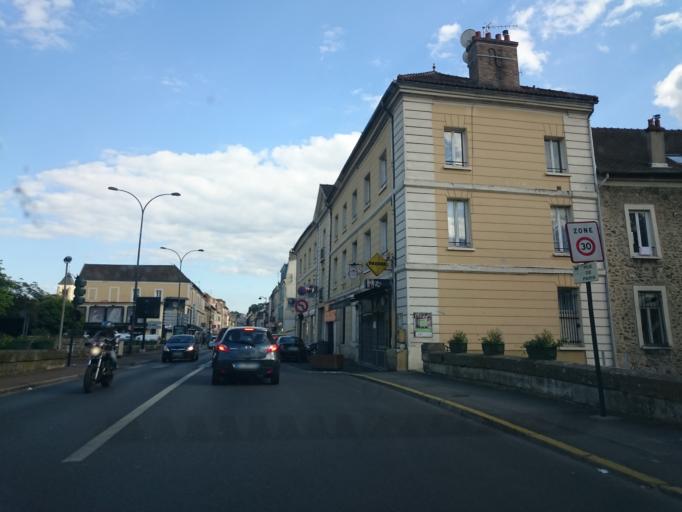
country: FR
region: Ile-de-France
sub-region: Departement de l'Essonne
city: Corbeil-Essonnes
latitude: 48.6053
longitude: 2.4669
